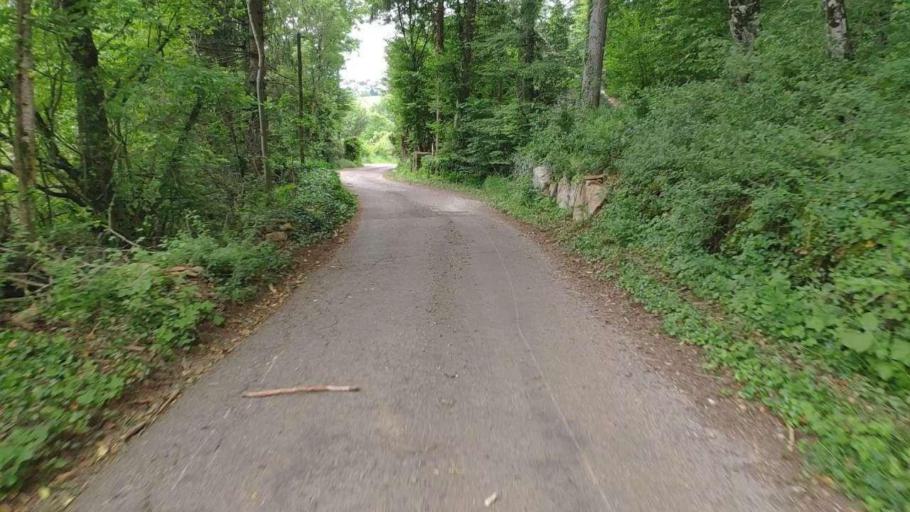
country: FR
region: Franche-Comte
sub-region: Departement du Jura
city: Montmorot
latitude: 46.7838
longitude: 5.5669
